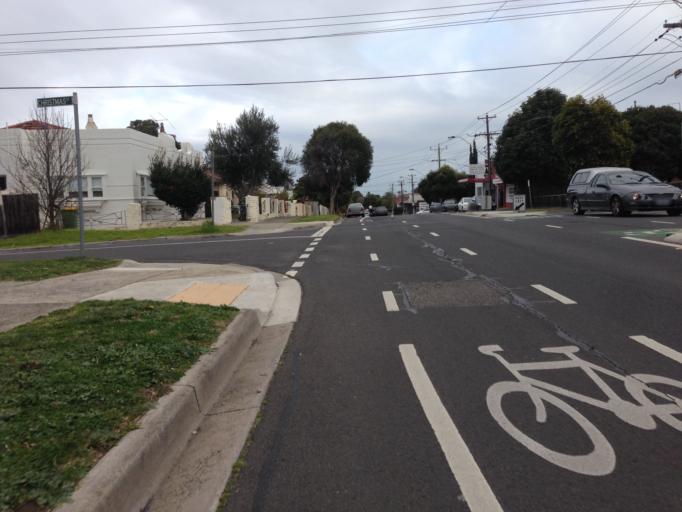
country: AU
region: Victoria
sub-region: Darebin
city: Thornbury
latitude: -37.7664
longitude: 145.0120
